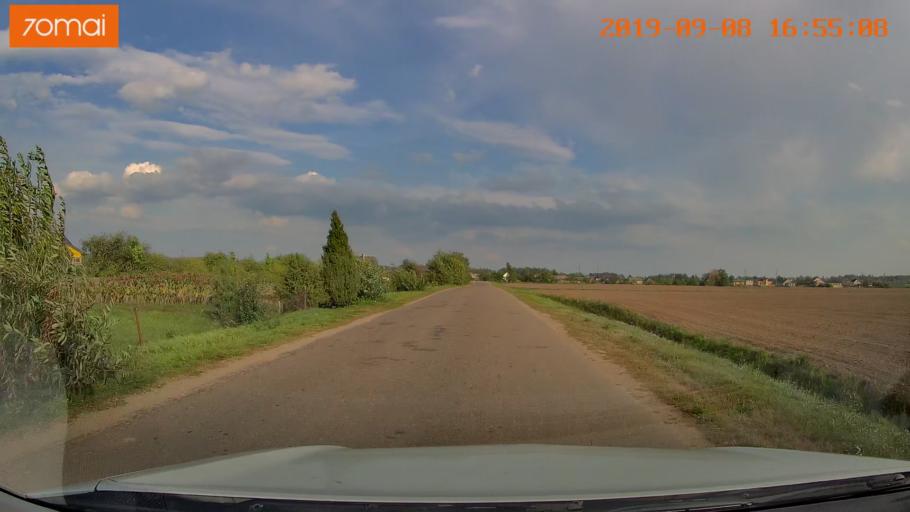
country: BY
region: Grodnenskaya
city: Hrodna
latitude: 53.7489
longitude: 23.9285
